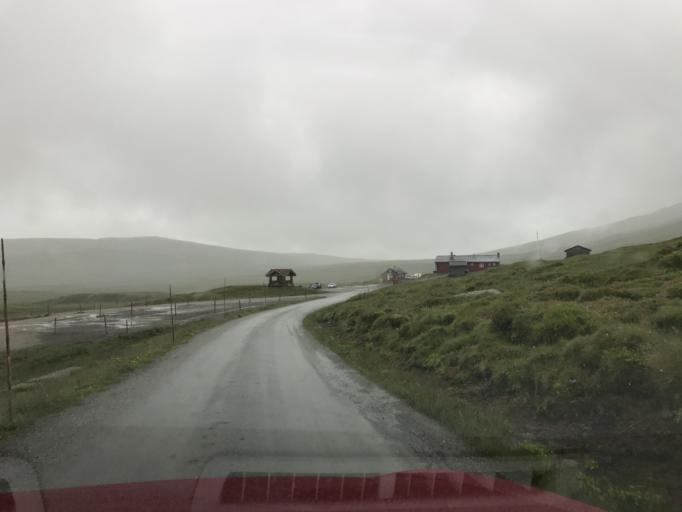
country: NO
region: Buskerud
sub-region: Hol
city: Geilo
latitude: 60.5502
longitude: 8.0709
